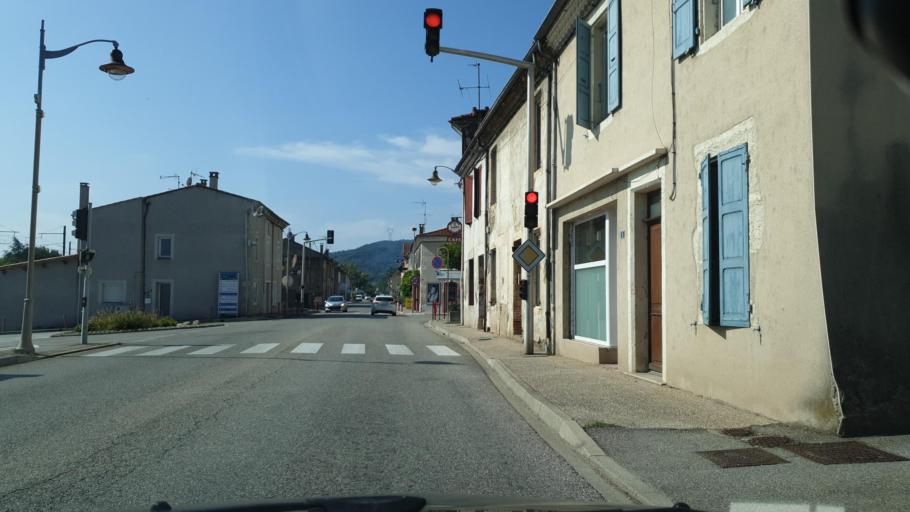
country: FR
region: Rhone-Alpes
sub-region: Departement de l'Ardeche
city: Beauchastel
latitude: 44.8264
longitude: 4.8030
